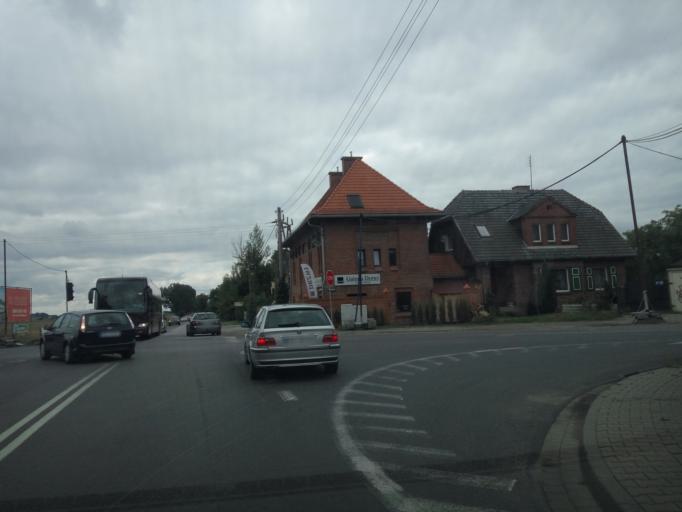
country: PL
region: Lower Silesian Voivodeship
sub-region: Powiat wroclawski
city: Zerniki Wroclawskie
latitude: 51.0508
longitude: 17.0310
